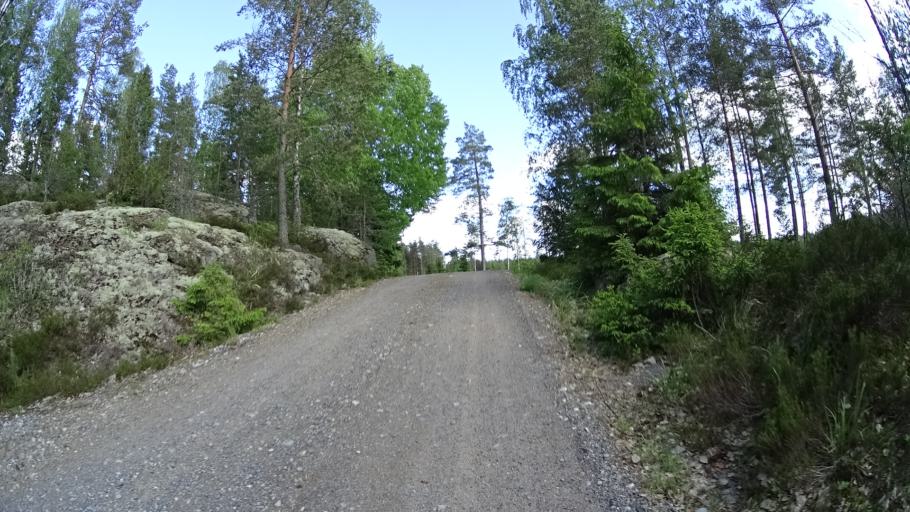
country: FI
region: Uusimaa
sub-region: Raaseporin
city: Pohja
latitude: 60.1562
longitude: 23.4888
